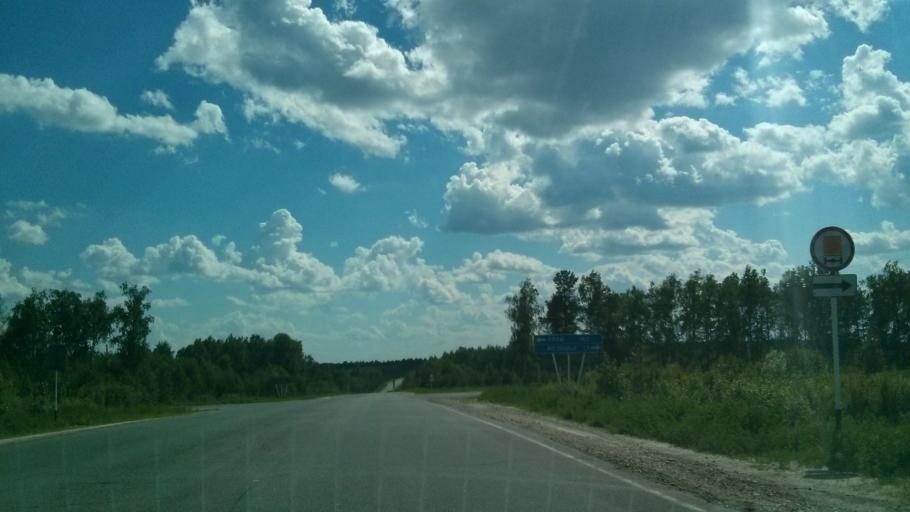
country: RU
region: Vladimir
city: Melenki
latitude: 55.3360
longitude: 41.6640
